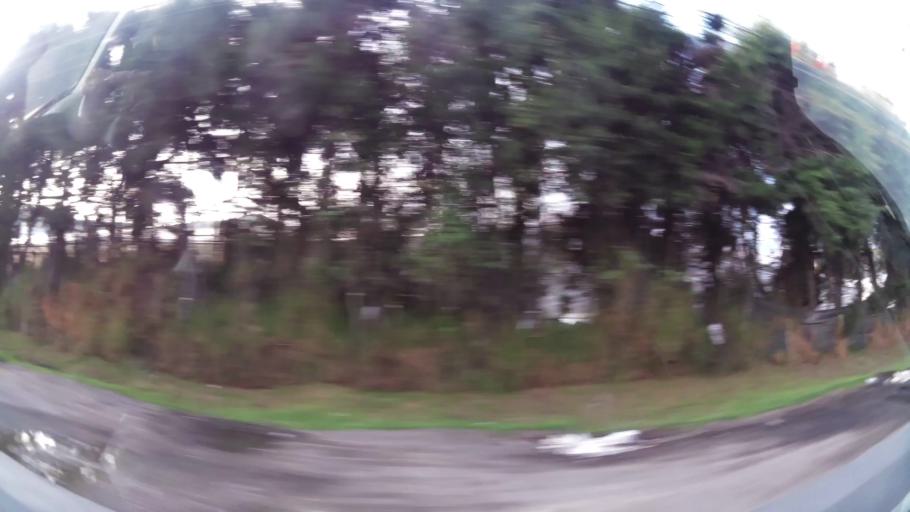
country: CO
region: Cundinamarca
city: Cota
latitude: 4.7812
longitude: -74.1350
